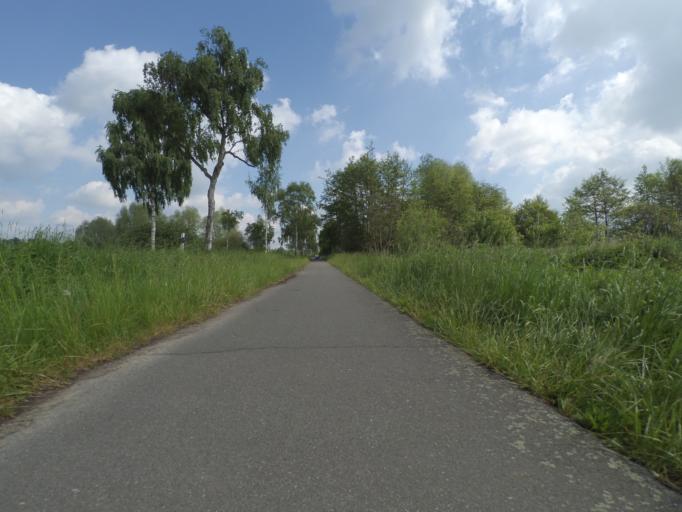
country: DE
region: Lower Saxony
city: Didderse
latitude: 52.3768
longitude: 10.3438
